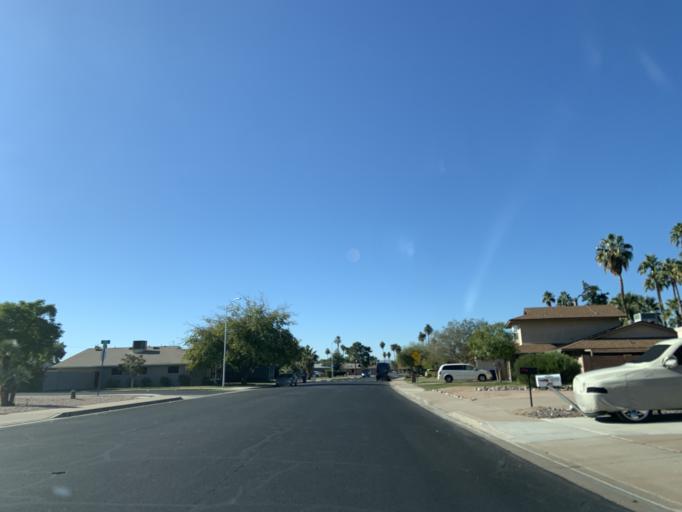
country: US
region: Arizona
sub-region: Maricopa County
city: San Carlos
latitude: 33.3601
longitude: -111.8611
